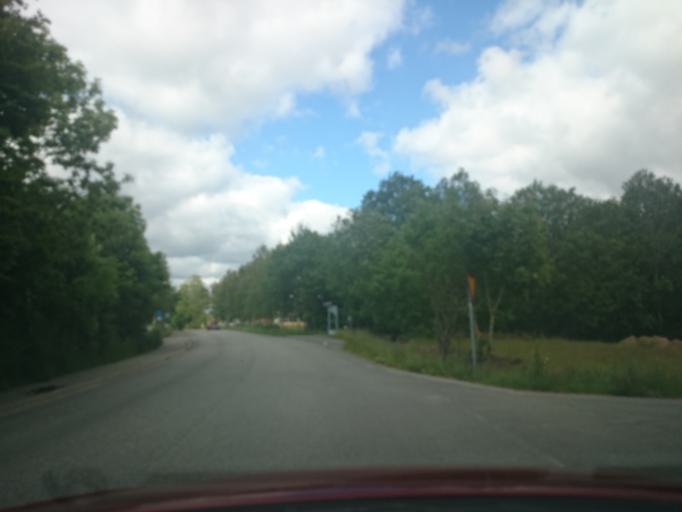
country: SE
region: Vaestra Goetaland
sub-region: Harryda Kommun
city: Landvetter
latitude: 57.6989
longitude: 12.1843
